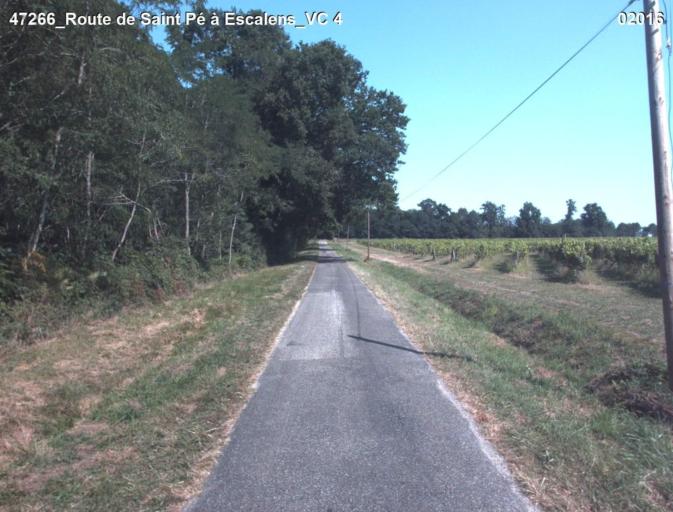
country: FR
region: Aquitaine
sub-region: Departement des Landes
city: Gabarret
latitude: 43.9997
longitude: 0.0847
